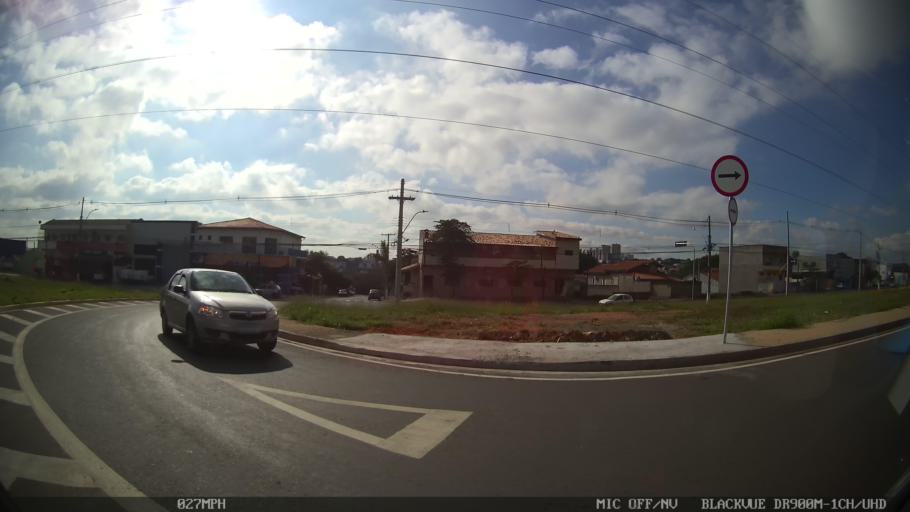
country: BR
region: Sao Paulo
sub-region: Hortolandia
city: Hortolandia
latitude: -22.9048
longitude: -47.1847
